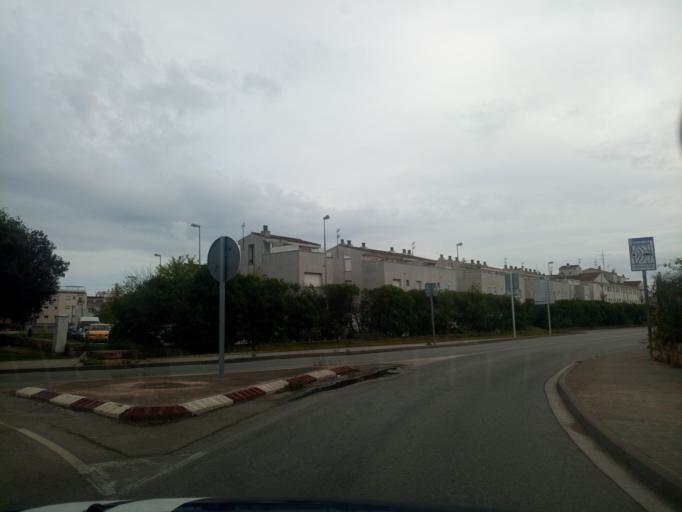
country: ES
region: Catalonia
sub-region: Provincia de Barcelona
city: Vilanova i la Geltru
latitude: 41.2263
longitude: 1.7531
